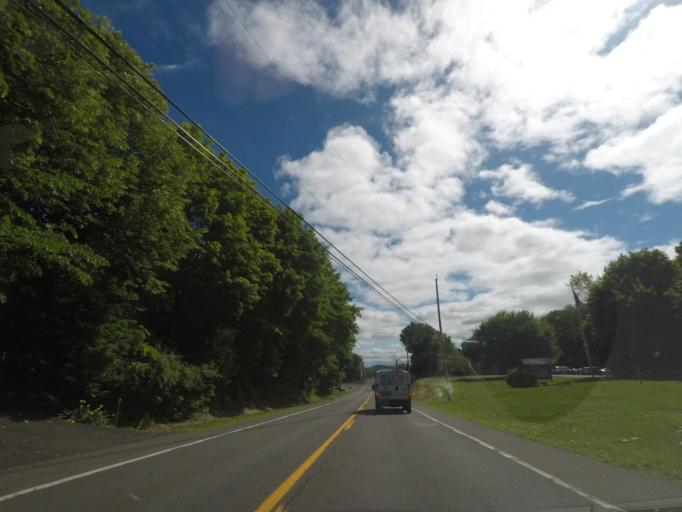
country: US
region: New York
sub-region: Dutchess County
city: Pine Plains
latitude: 42.1088
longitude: -73.5379
